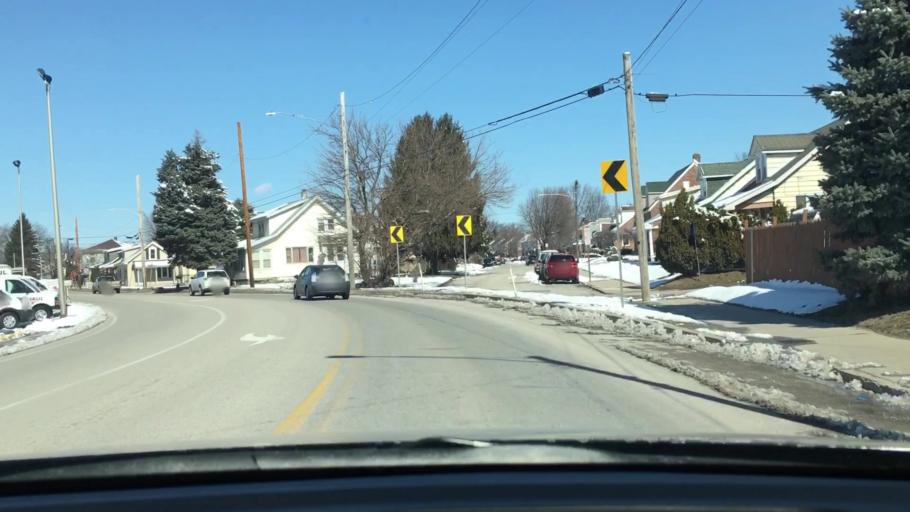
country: US
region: Pennsylvania
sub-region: York County
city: West York
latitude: 39.9707
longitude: -76.7514
